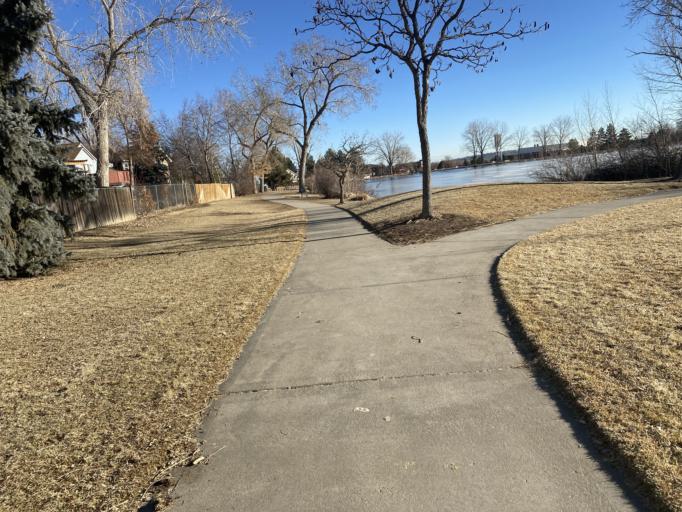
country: US
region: Colorado
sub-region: Jefferson County
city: Applewood
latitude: 39.8092
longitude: -105.1446
